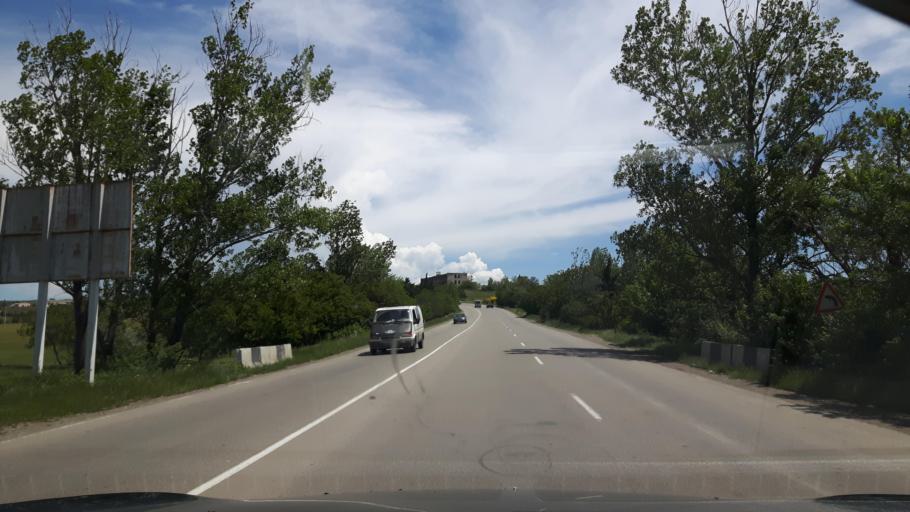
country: GE
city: Didi Lilo
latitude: 41.6927
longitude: 45.0345
